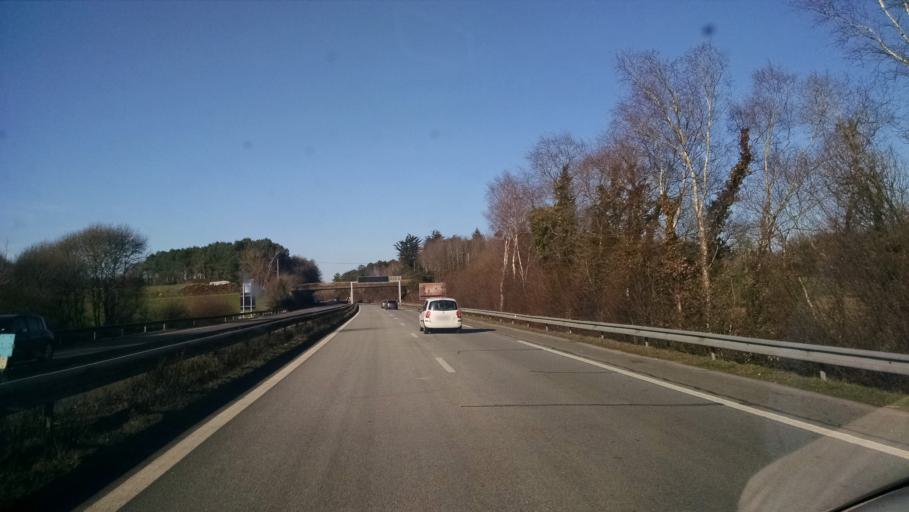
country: FR
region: Brittany
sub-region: Departement du Morbihan
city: Branderion
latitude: 47.7830
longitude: -3.2071
